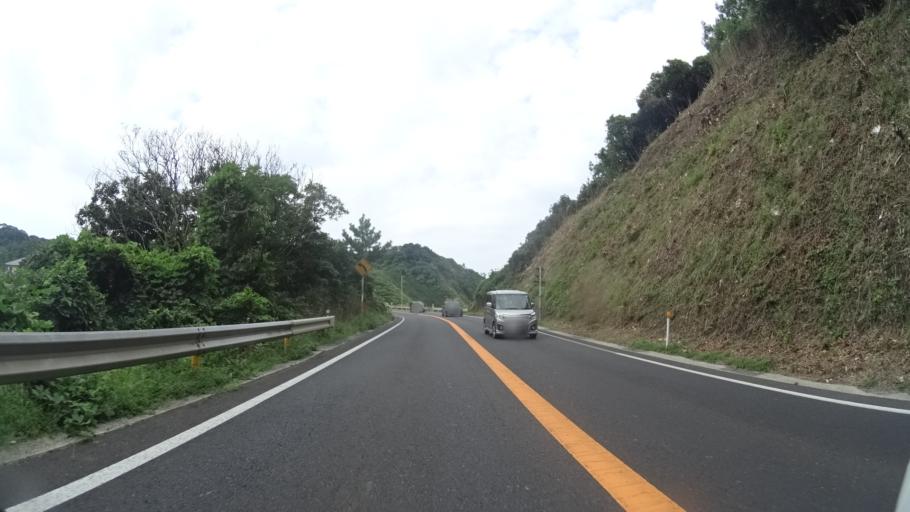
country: JP
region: Shimane
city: Odacho-oda
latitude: 35.1934
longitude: 132.4388
